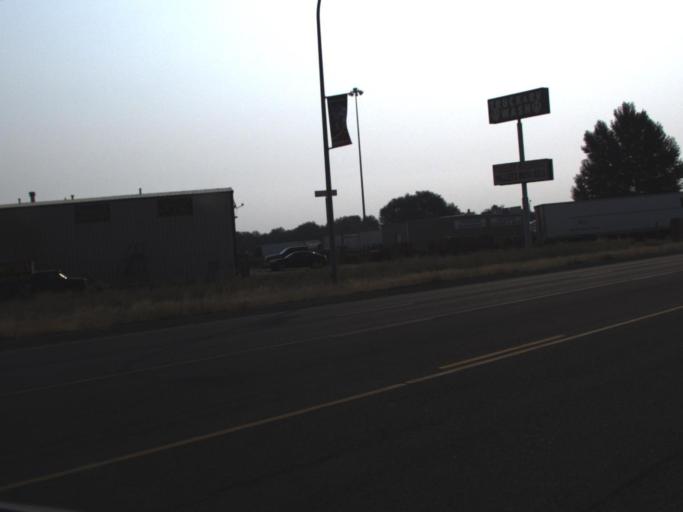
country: US
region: Washington
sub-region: Kittitas County
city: Ellensburg
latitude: 47.0088
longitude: -120.5887
